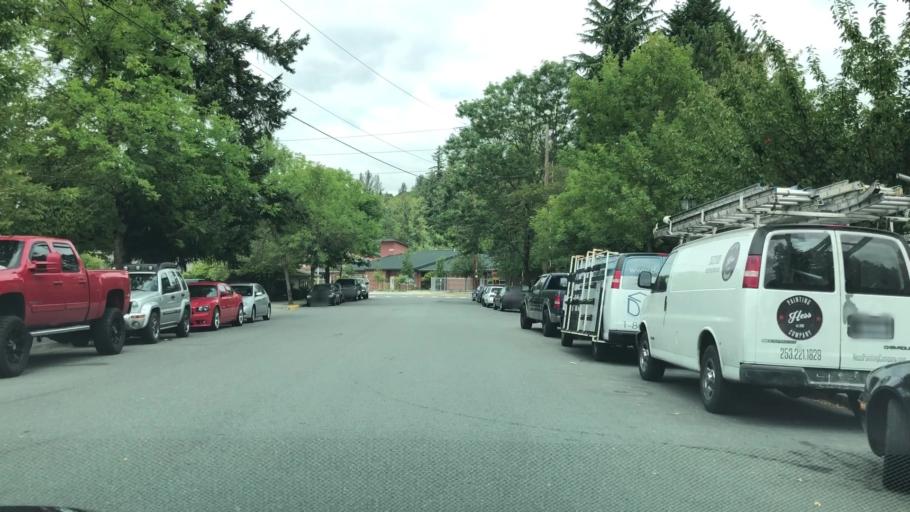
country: US
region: Washington
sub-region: King County
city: Redmond
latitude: 47.6738
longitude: -122.1163
